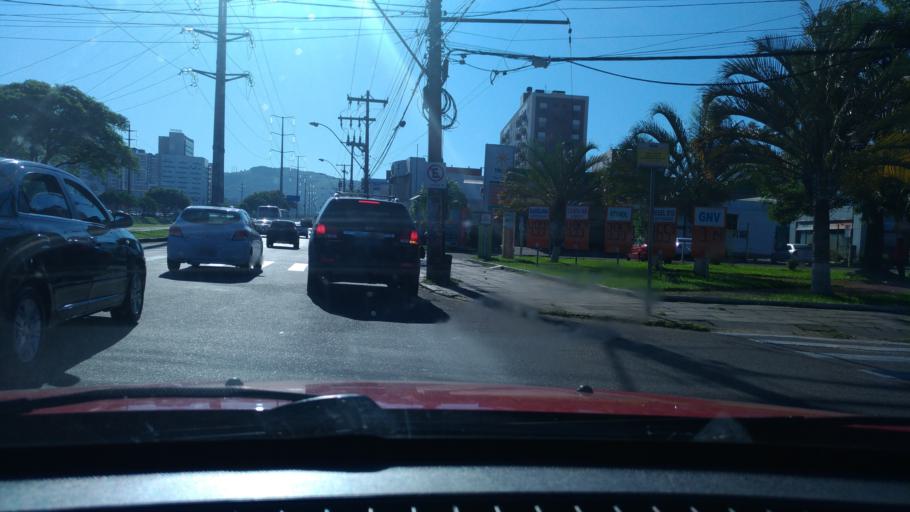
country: BR
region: Rio Grande do Sul
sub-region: Porto Alegre
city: Porto Alegre
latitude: -30.0560
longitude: -51.1692
